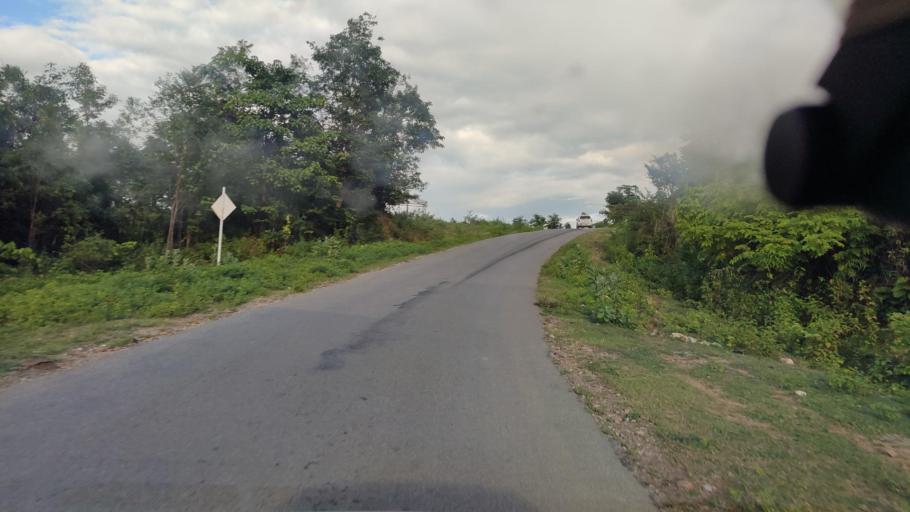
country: MM
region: Magway
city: Taungdwingyi
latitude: 20.0157
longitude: 95.8305
